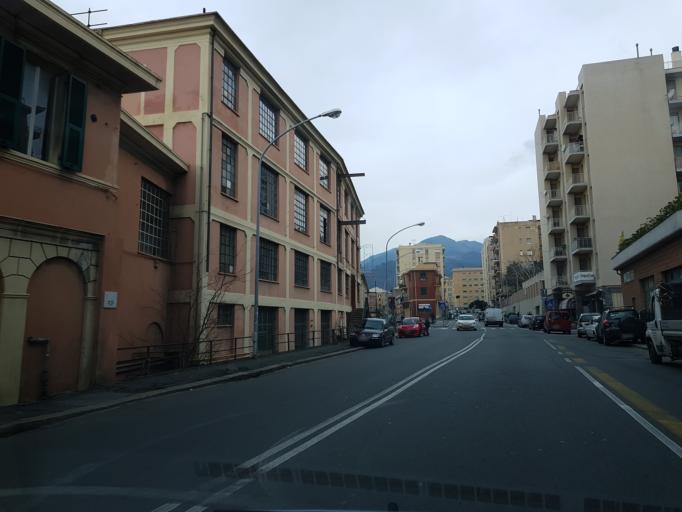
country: IT
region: Liguria
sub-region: Provincia di Genova
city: Mele
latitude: 44.4284
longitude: 8.7622
